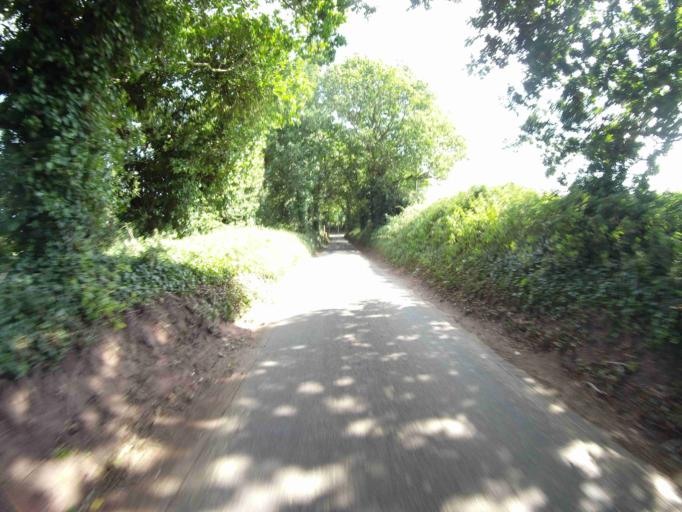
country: GB
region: England
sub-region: Devon
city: Budleigh Salterton
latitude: 50.6387
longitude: -3.3399
